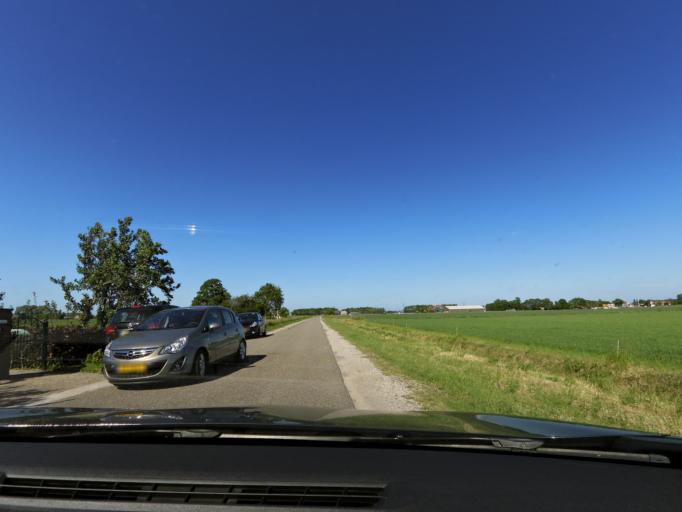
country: NL
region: South Holland
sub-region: Gemeente Hellevoetsluis
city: Nieuwenhoorn
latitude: 51.8678
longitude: 4.1517
